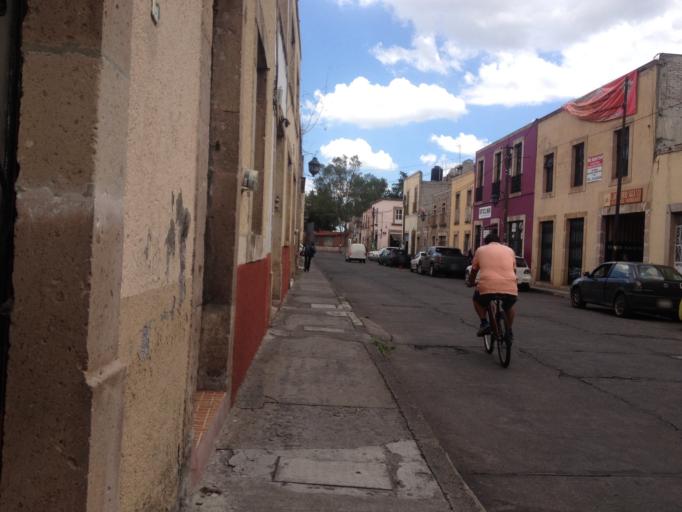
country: MX
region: Michoacan
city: Morelia
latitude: 19.7054
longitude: -101.1823
